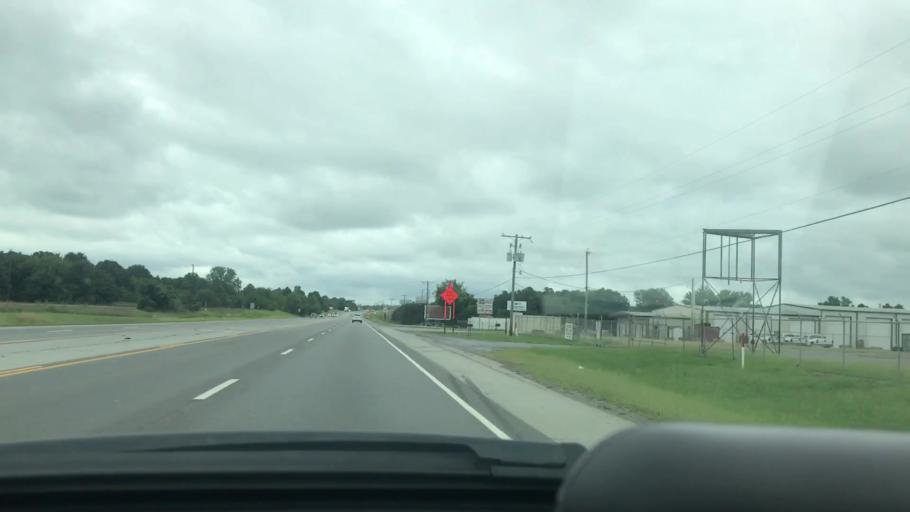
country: US
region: Oklahoma
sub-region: Pittsburg County
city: McAlester
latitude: 34.8786
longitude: -95.7962
